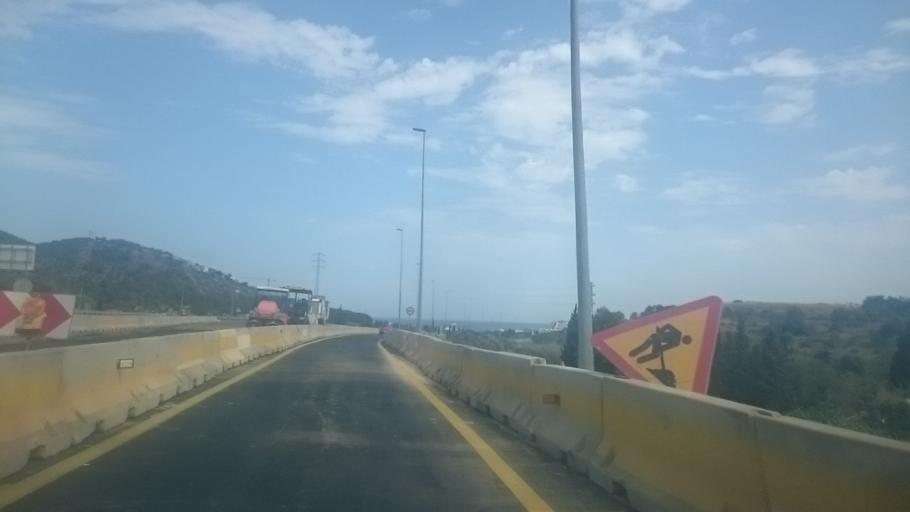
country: ES
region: Catalonia
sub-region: Provincia de Barcelona
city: Sitges
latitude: 41.2458
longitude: 1.8128
